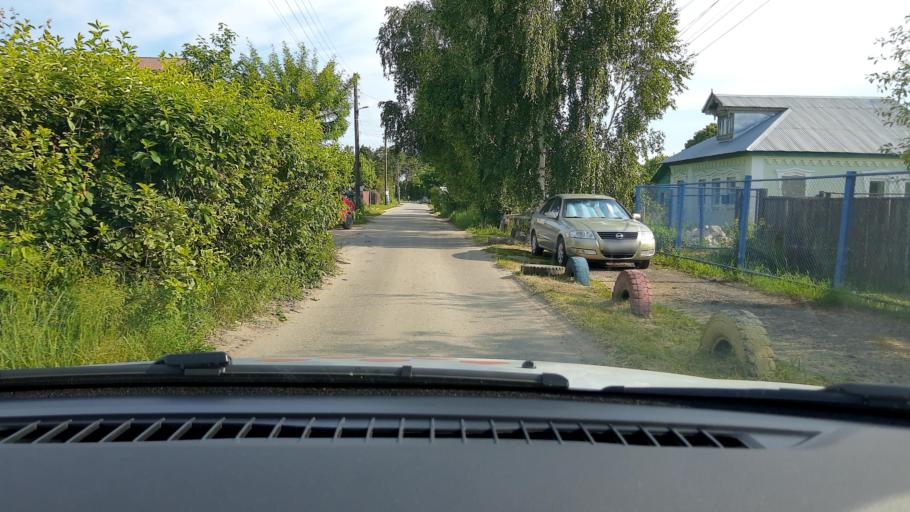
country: RU
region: Nizjnij Novgorod
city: Gorbatovka
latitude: 56.2617
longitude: 43.7463
